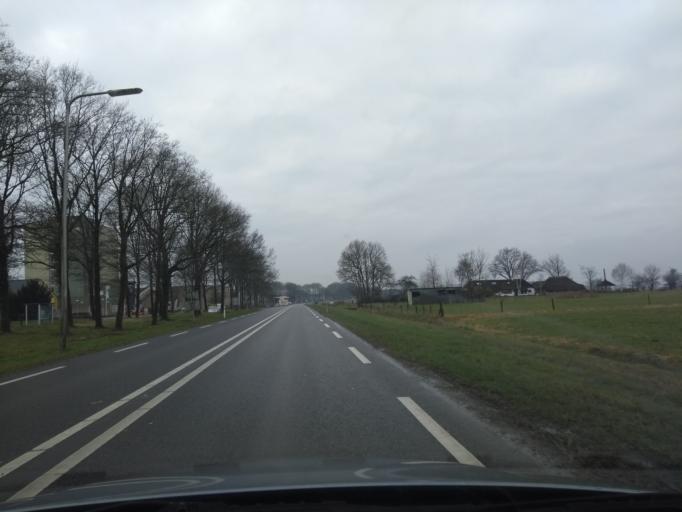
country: NL
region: Overijssel
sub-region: Gemeente Steenwijkerland
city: Vollenhove
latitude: 52.6833
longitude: 5.9637
